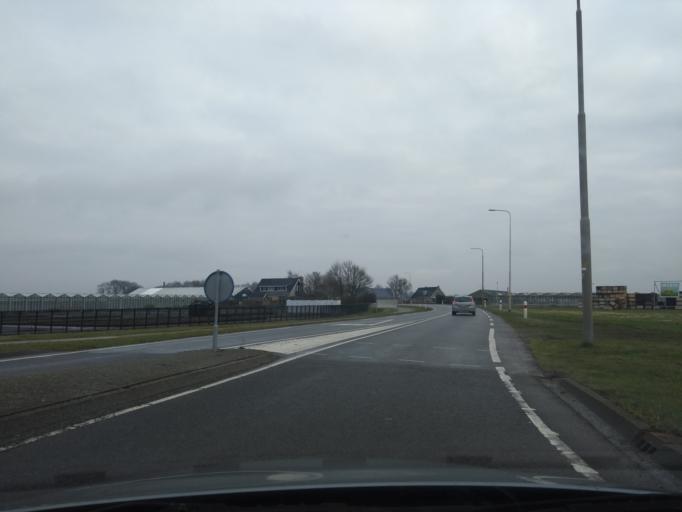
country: NL
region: Flevoland
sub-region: Gemeente Noordoostpolder
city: Ens
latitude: 52.7130
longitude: 5.8681
